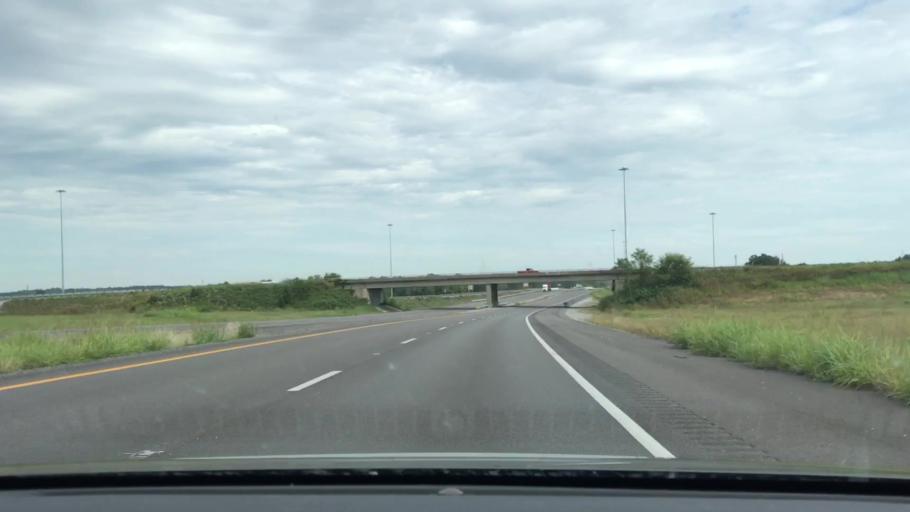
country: US
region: Kentucky
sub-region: Marshall County
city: Benton
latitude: 36.8672
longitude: -88.3658
